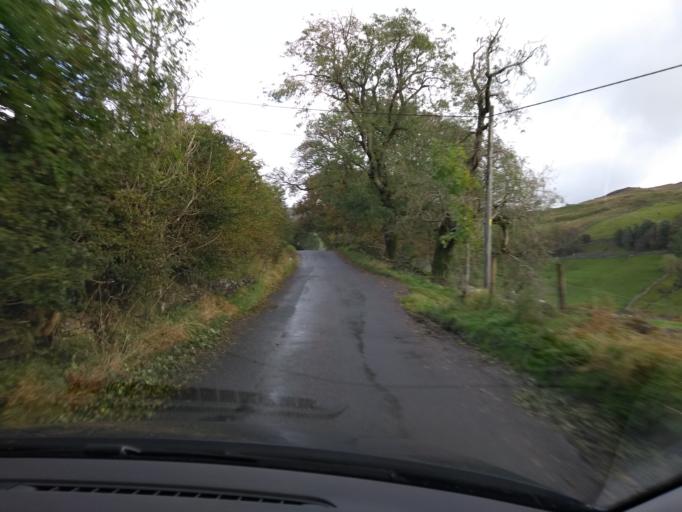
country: GB
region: England
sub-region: Cumbria
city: Kirkby Stephen
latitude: 54.3985
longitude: -2.1713
